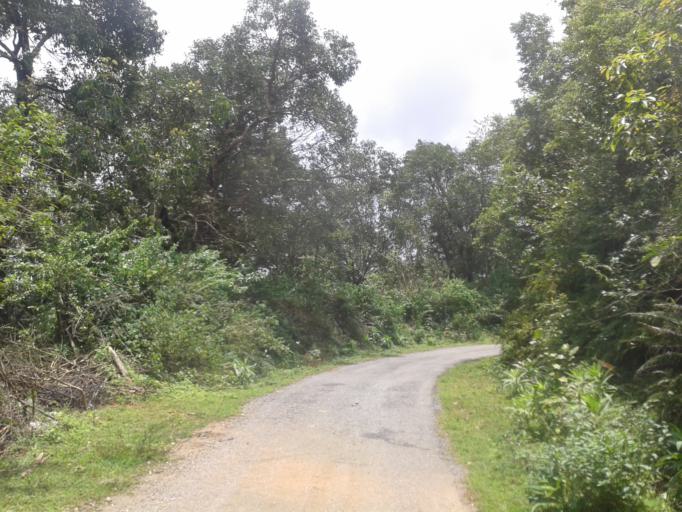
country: IN
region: Karnataka
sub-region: Chikmagalur
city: Mudigere
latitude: 12.9863
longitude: 75.6038
